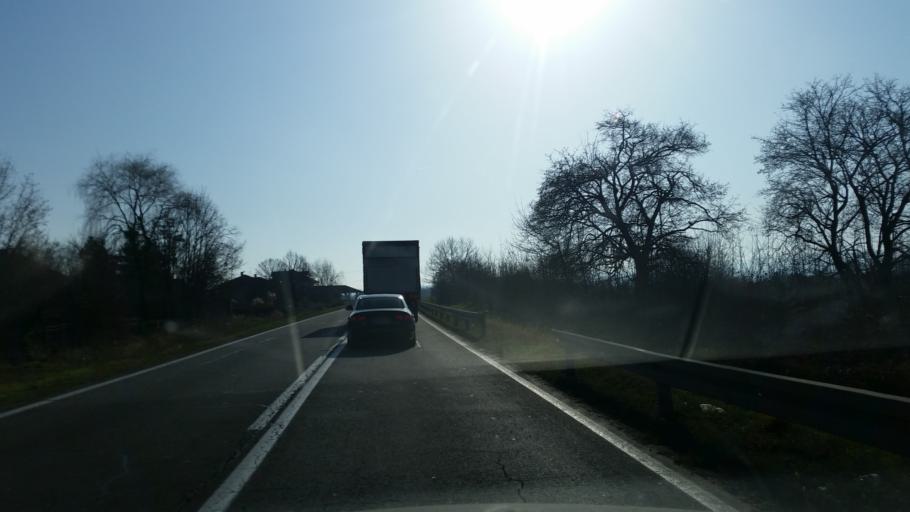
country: RS
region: Central Serbia
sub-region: Kolubarski Okrug
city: Ljig
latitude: 44.2784
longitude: 20.2800
